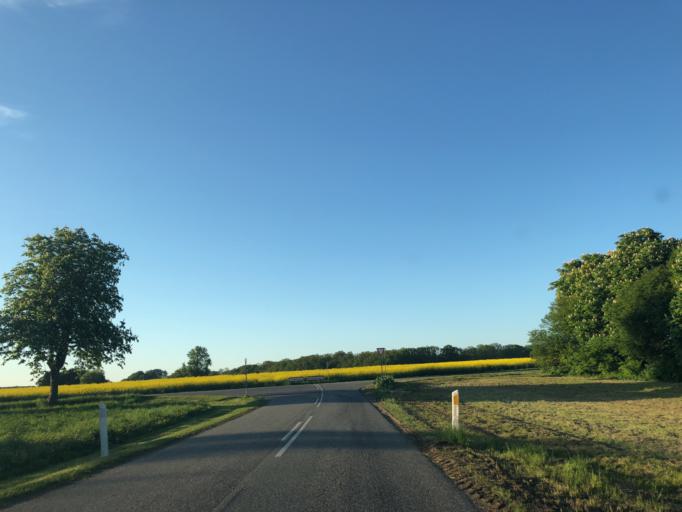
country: DK
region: Zealand
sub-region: Koge Kommune
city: Ejby
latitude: 55.4234
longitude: 12.0904
